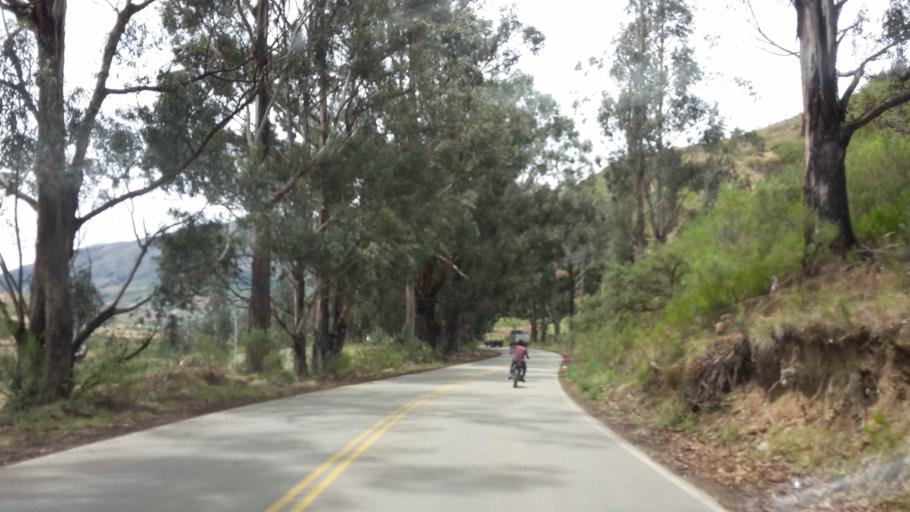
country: BO
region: Cochabamba
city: Totora
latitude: -17.6563
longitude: -65.2278
